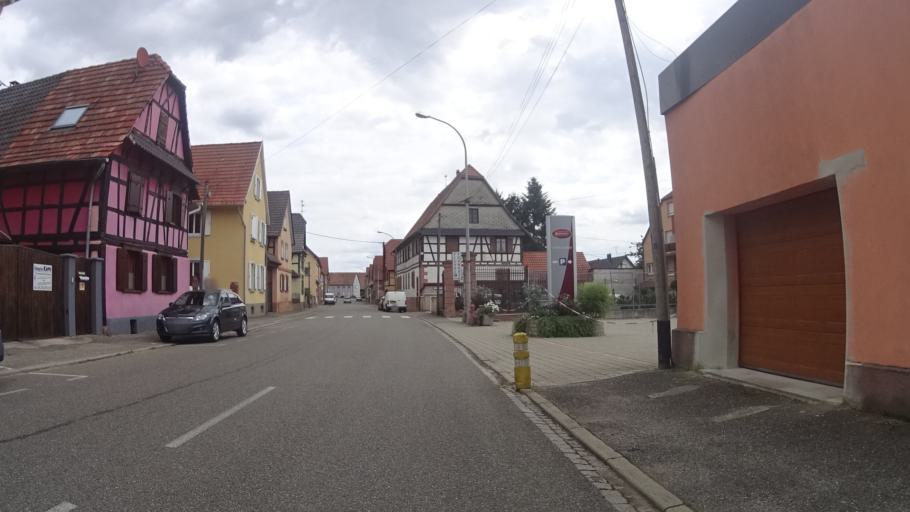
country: FR
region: Alsace
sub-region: Departement du Bas-Rhin
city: Geudertheim
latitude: 48.7226
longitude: 7.7486
